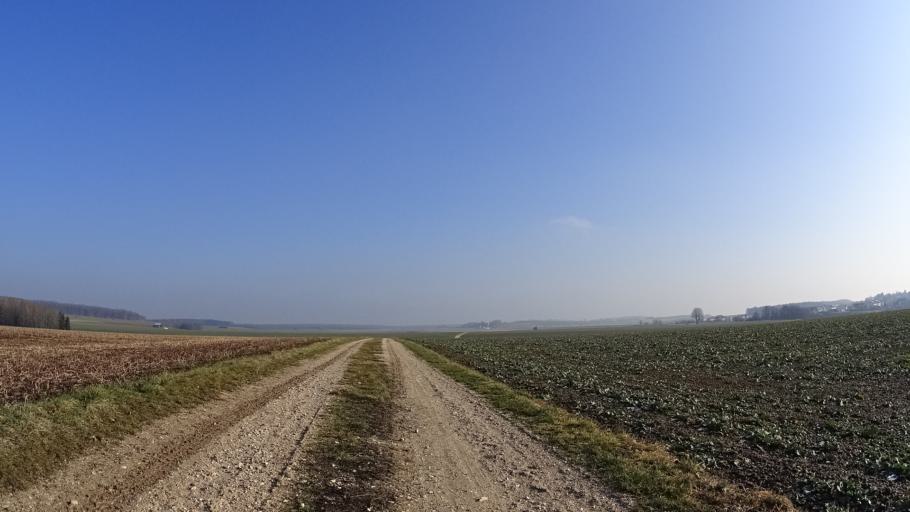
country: DE
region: Bavaria
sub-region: Upper Bavaria
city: Hepberg
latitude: 48.8249
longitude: 11.4942
